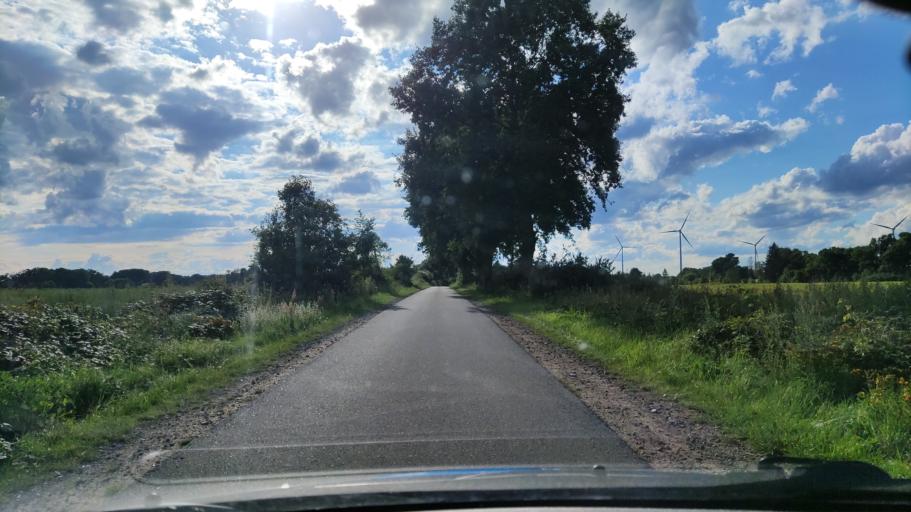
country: DE
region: Lower Saxony
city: Nahrendorf
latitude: 53.1791
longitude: 10.7928
